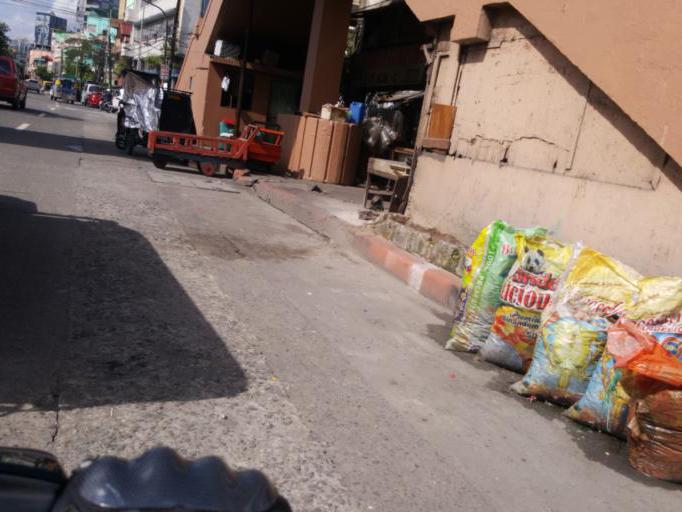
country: PH
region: Metro Manila
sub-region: City of Manila
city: Manila
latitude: 14.6066
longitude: 120.9859
